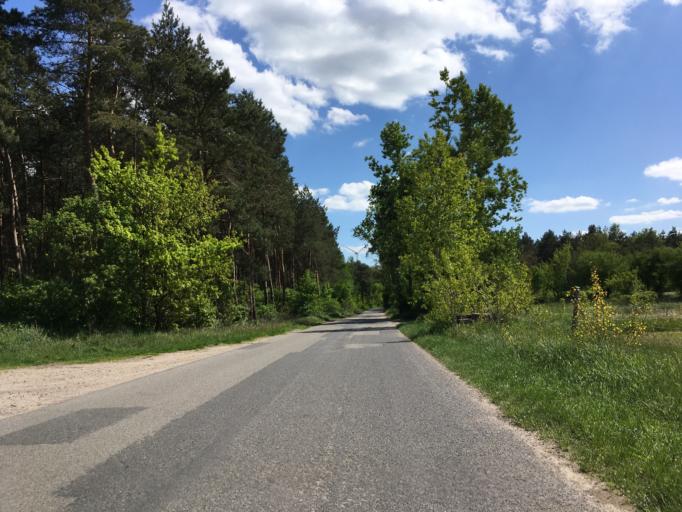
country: DE
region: Brandenburg
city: Rudnitz
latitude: 52.6989
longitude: 13.6665
